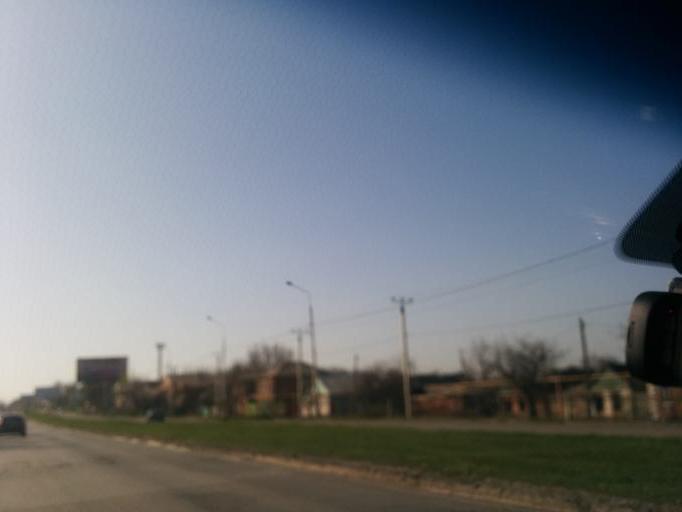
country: RU
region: Rostov
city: Shakhty
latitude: 47.7107
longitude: 40.1674
